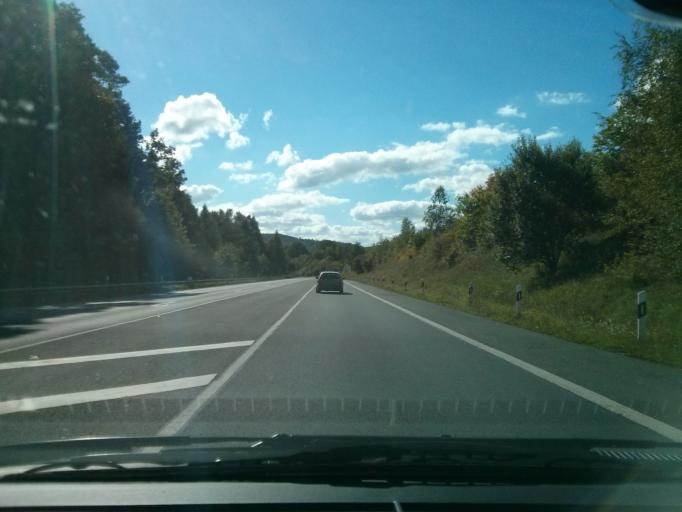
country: DE
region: North Rhine-Westphalia
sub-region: Regierungsbezirk Arnsberg
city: Arnsberg
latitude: 51.4222
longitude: 8.0582
